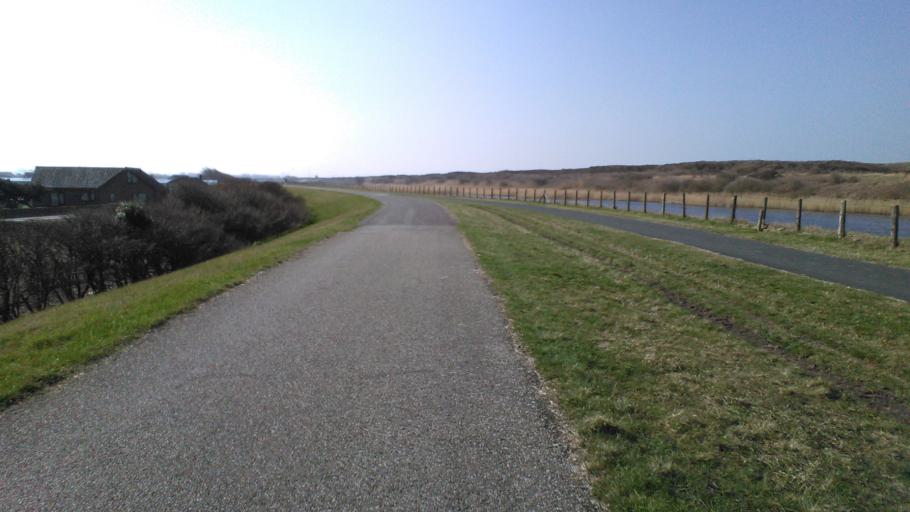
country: NL
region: South Holland
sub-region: Gemeente Westland
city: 's-Gravenzande
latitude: 52.0077
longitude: 4.1426
